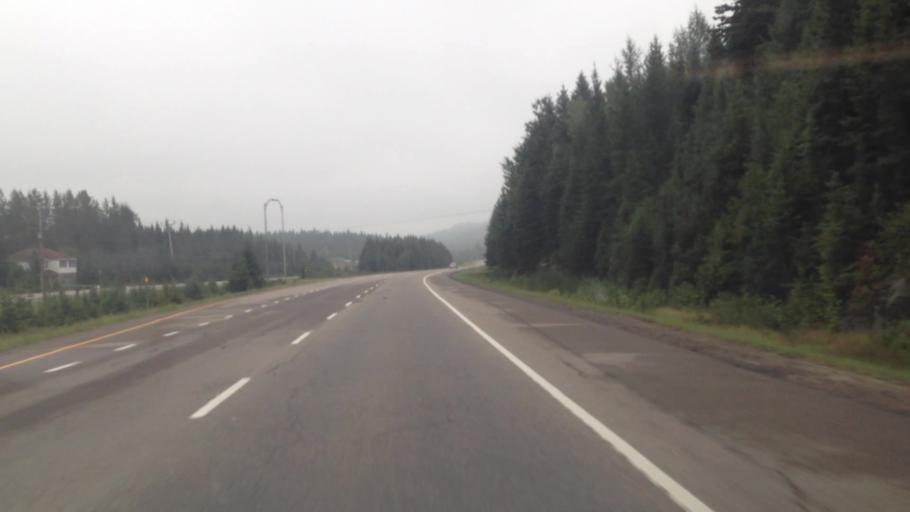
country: CA
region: Quebec
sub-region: Laurentides
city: Sainte-Agathe-des-Monts
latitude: 46.1025
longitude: -74.3834
